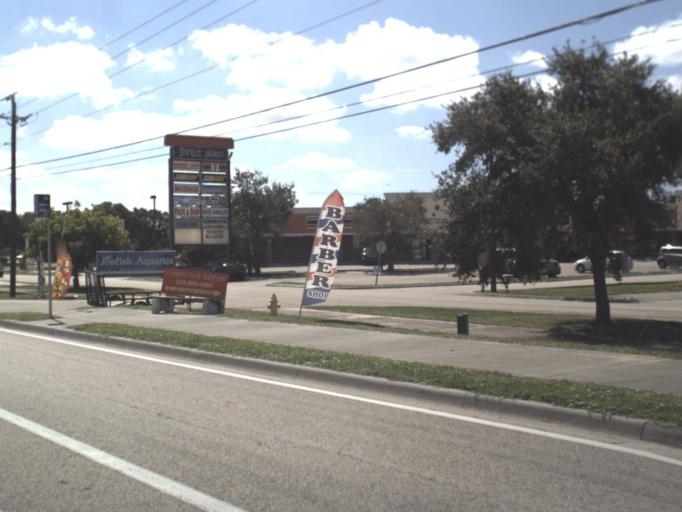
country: US
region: Florida
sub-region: Lee County
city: Villas
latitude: 26.5040
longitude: -81.8576
